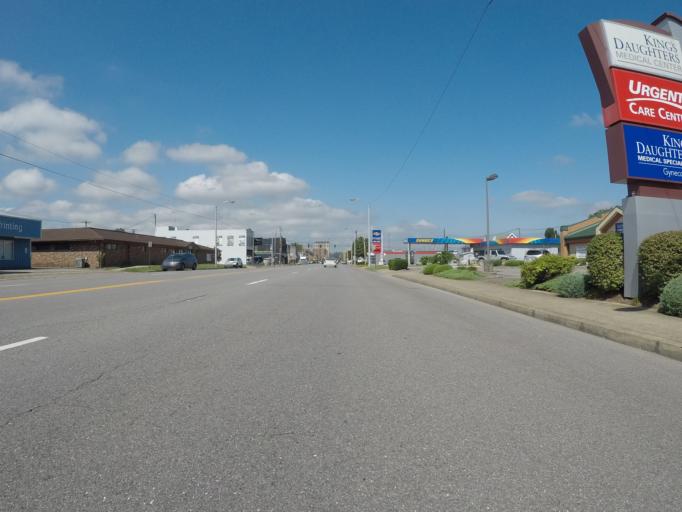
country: US
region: Kentucky
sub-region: Boyd County
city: Ashland
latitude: 38.4745
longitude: -82.6311
